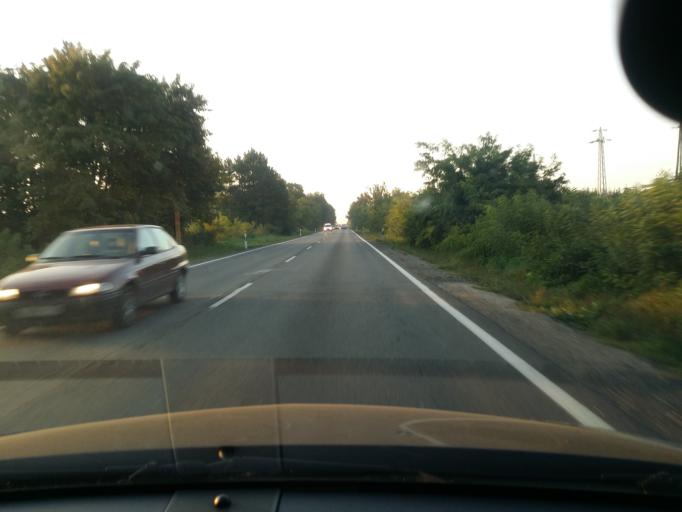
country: HU
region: Fejer
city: dunaujvaros
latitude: 46.9572
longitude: 18.9106
